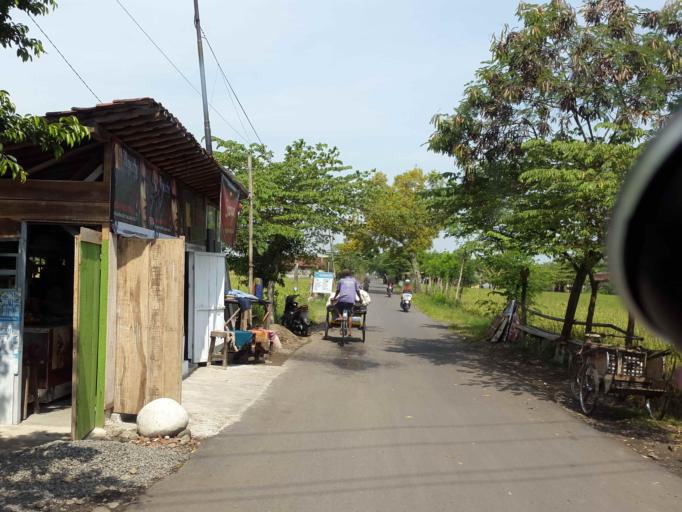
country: ID
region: Central Java
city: Pemalang
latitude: -6.8945
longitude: 109.3722
